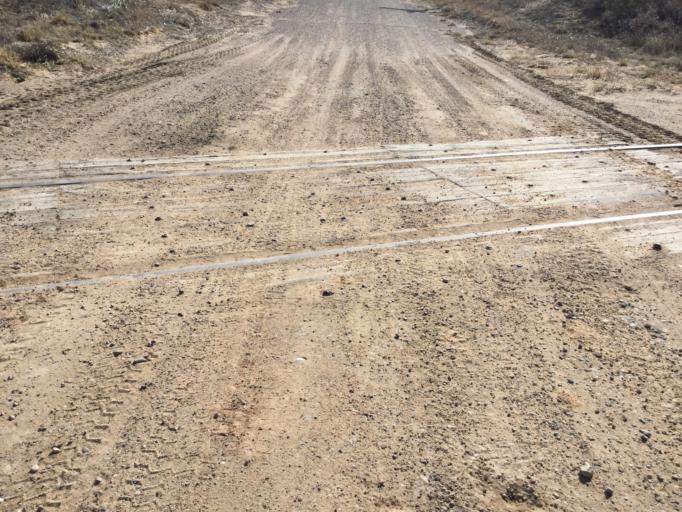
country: US
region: Kansas
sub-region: Morton County
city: Elkhart
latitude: 37.1015
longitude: -101.7003
